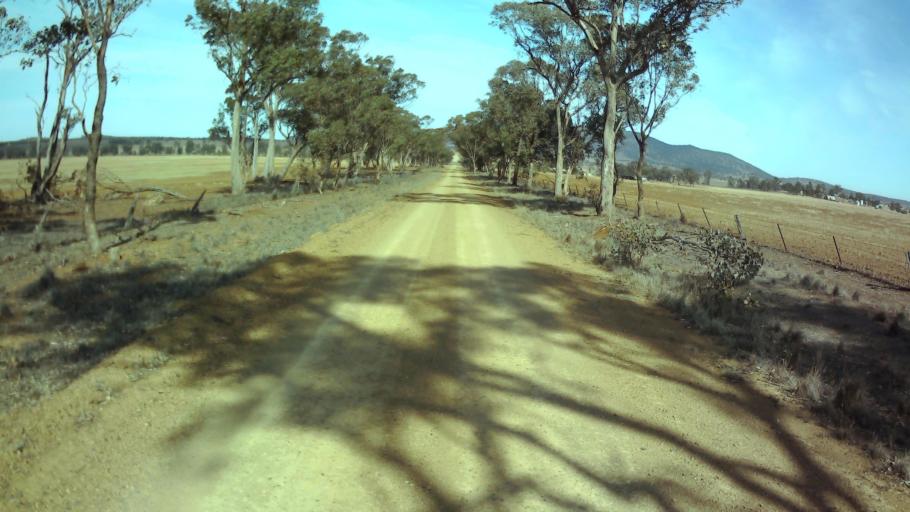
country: AU
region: New South Wales
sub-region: Weddin
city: Grenfell
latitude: -33.7518
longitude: 148.0026
